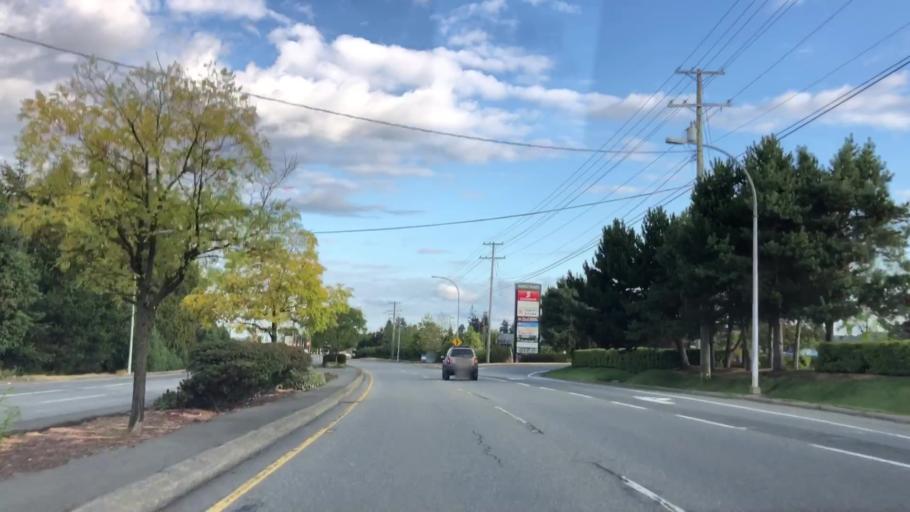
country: CA
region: British Columbia
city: Nanaimo
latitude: 49.2364
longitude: -124.0459
